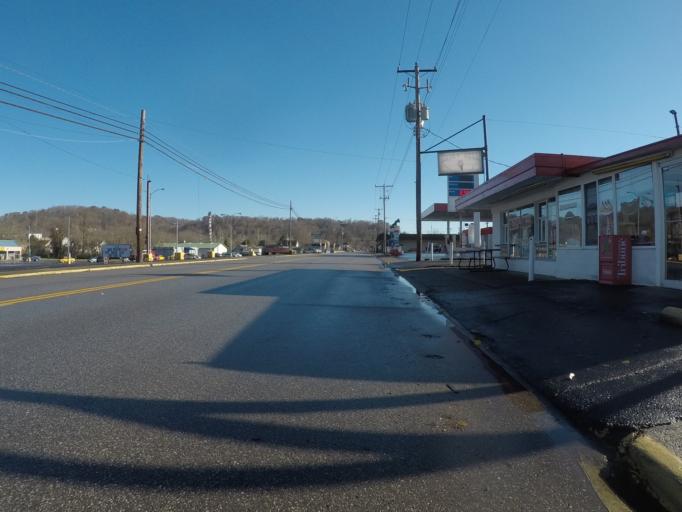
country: US
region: West Virginia
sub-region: Cabell County
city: Huntington
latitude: 38.4274
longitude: -82.4592
